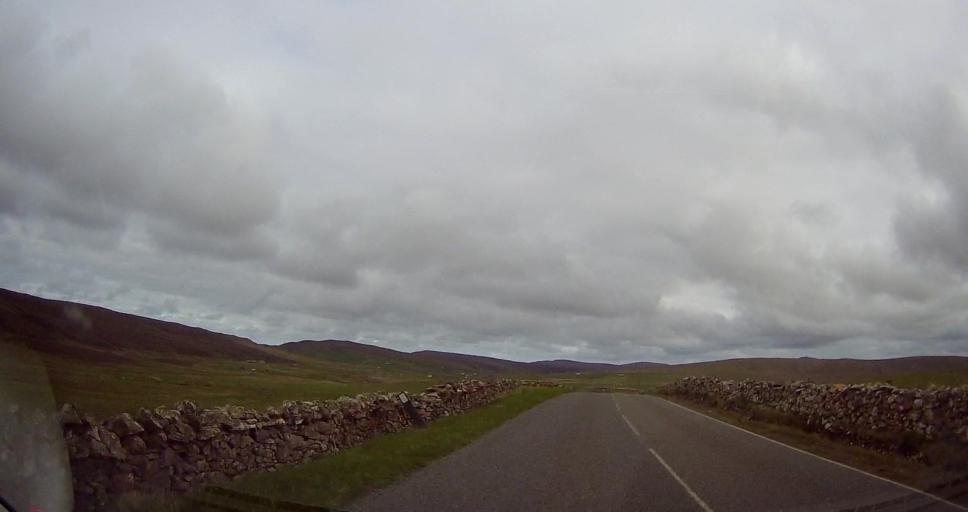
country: GB
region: Scotland
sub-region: Shetland Islands
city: Shetland
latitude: 60.7479
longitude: -0.8851
